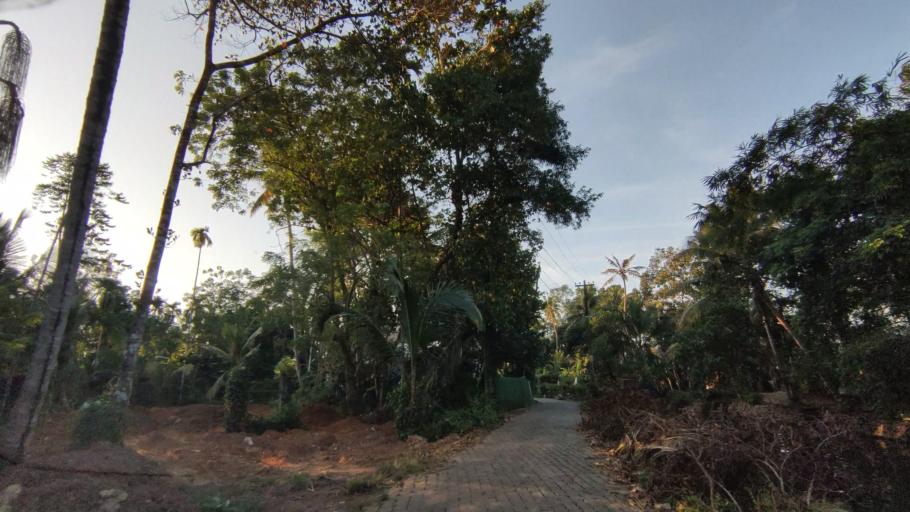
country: IN
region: Kerala
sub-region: Kottayam
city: Kottayam
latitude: 9.6309
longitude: 76.4838
